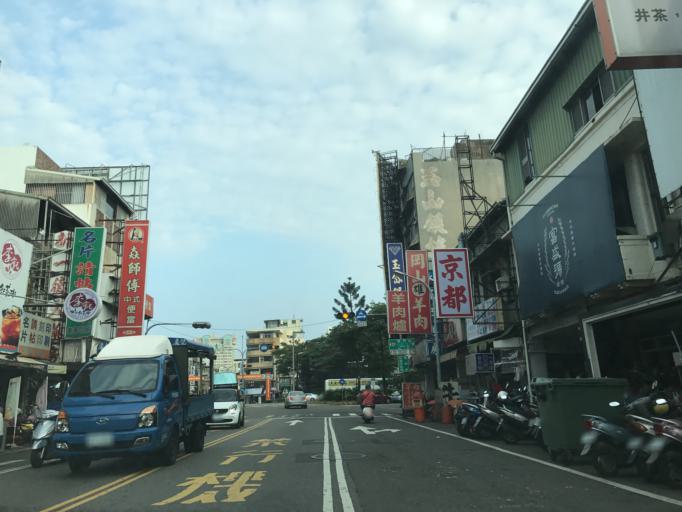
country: TW
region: Taiwan
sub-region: Tainan
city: Tainan
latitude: 22.9977
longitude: 120.1991
